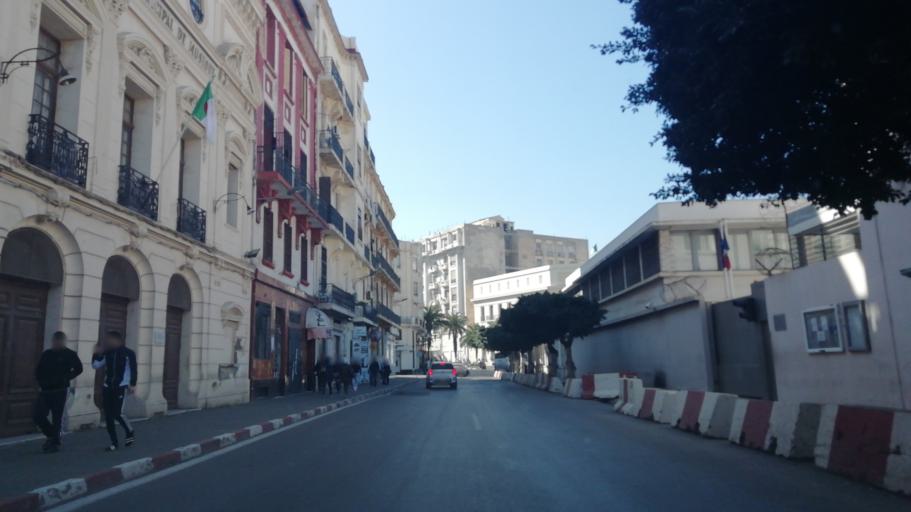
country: DZ
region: Oran
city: Oran
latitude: 35.7043
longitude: -0.6446
